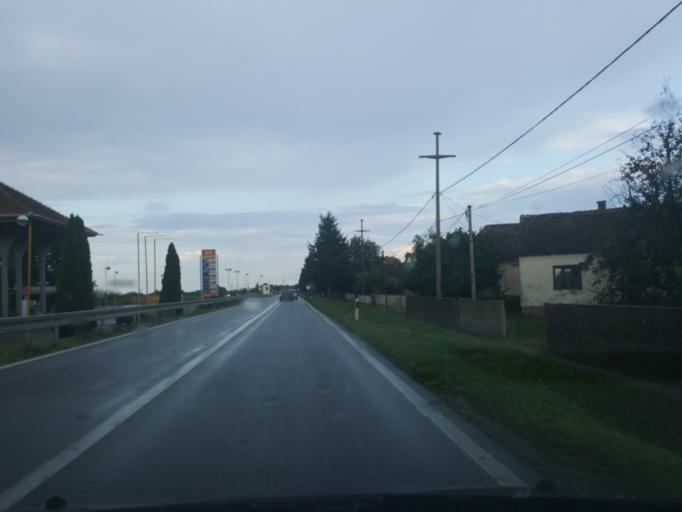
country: RS
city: Zminjak
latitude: 44.7330
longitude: 19.4649
